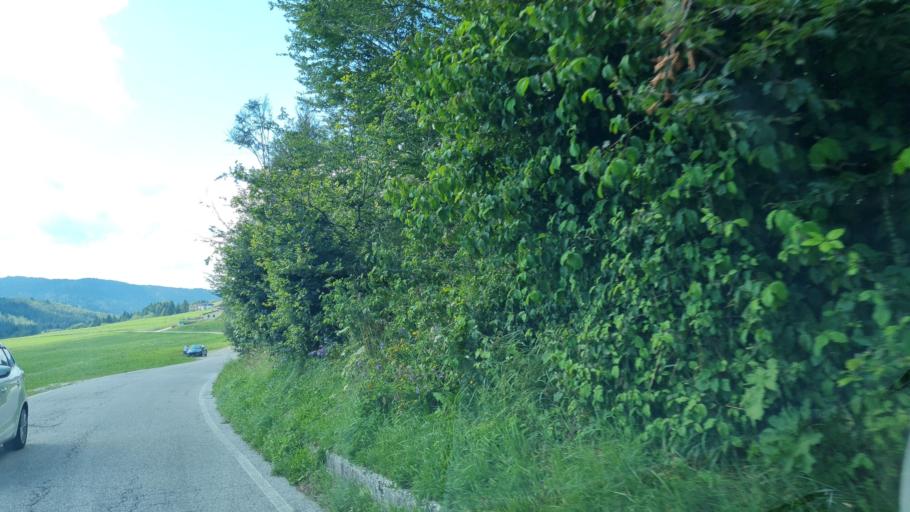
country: IT
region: Veneto
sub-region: Provincia di Vicenza
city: Conco
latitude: 45.8157
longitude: 11.6407
